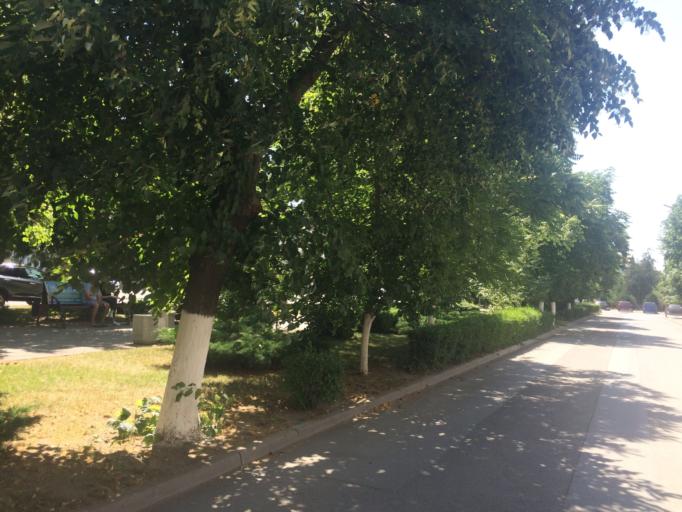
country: RU
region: Rostov
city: Sal'sk
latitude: 46.4718
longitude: 41.5446
